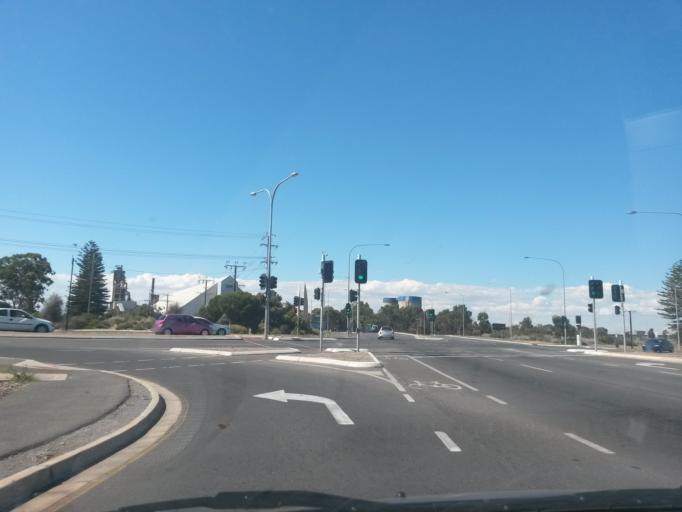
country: AU
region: South Australia
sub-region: Port Adelaide Enfield
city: Birkenhead
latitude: -34.8395
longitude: 138.5018
